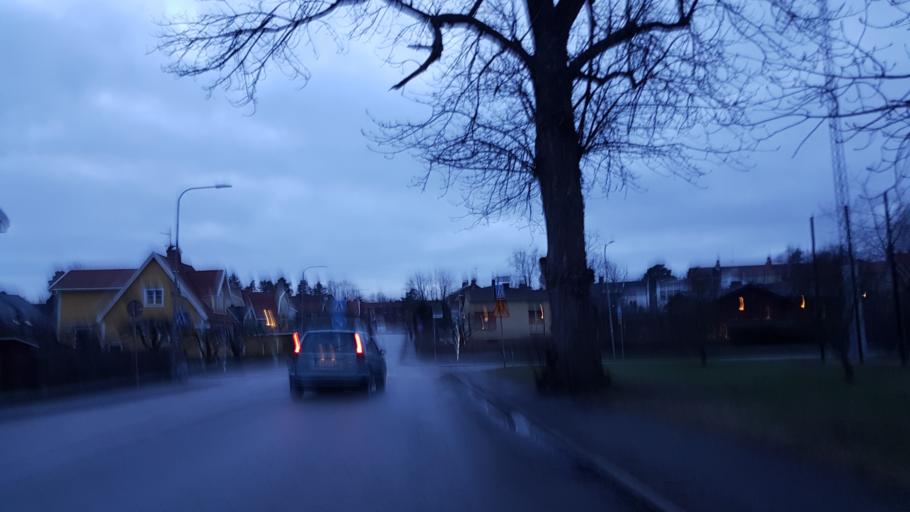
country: SE
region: Stockholm
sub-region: Stockholms Kommun
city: Arsta
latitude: 59.2796
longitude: 18.0495
